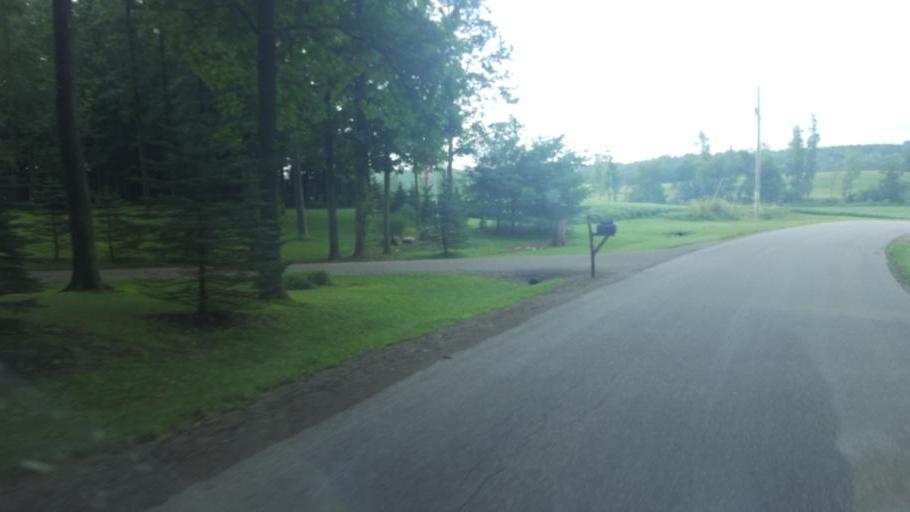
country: US
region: Ohio
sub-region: Knox County
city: Fredericktown
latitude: 40.4568
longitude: -82.6777
